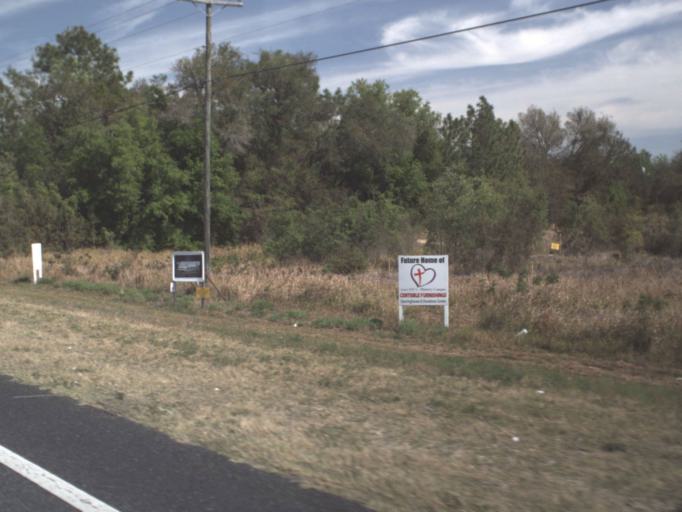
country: US
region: Florida
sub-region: Sumter County
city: The Villages
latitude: 28.9933
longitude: -81.9955
